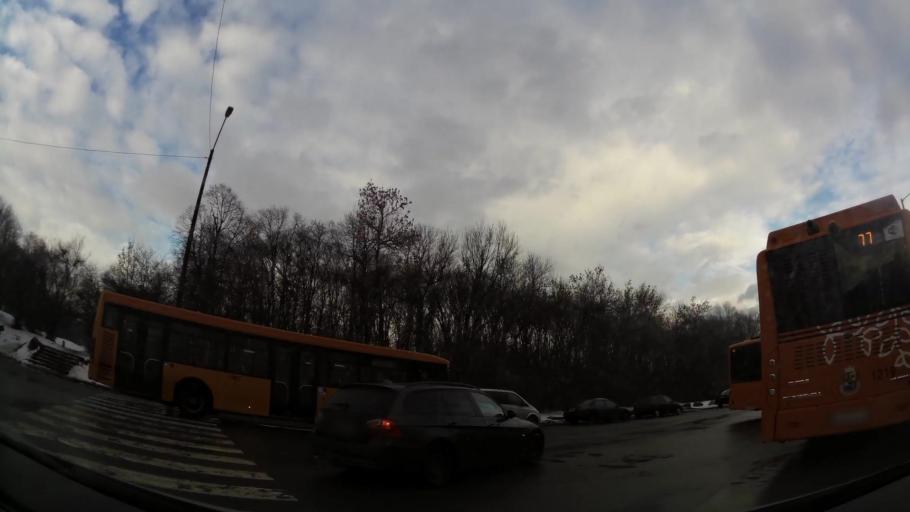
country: BG
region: Sofia-Capital
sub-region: Stolichna Obshtina
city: Sofia
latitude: 42.7014
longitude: 23.2760
